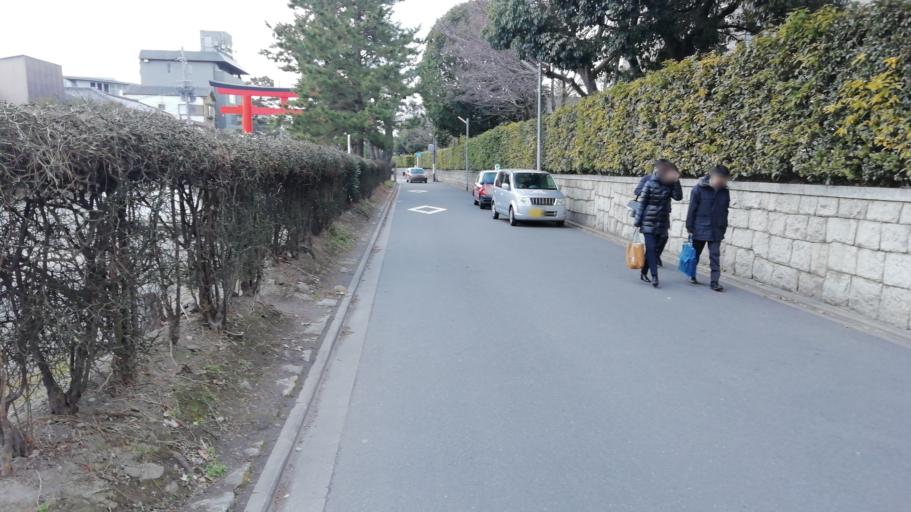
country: JP
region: Kyoto
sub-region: Kyoto-shi
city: Kamigyo-ku
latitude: 35.0253
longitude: 135.7827
